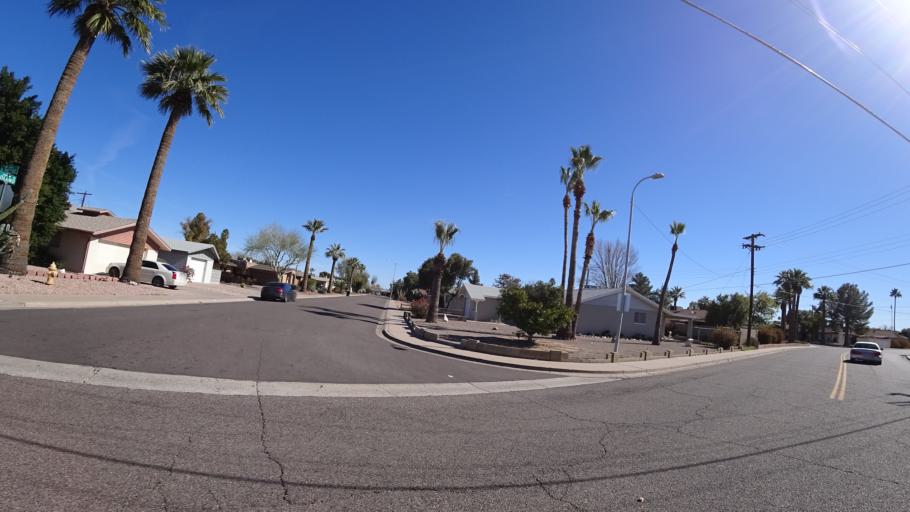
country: US
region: Arizona
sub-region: Maricopa County
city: Scottsdale
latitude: 33.5210
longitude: -111.8963
